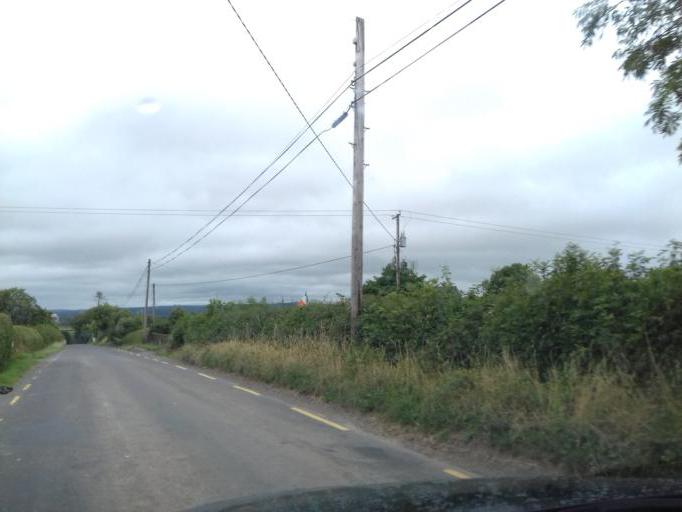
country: IE
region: Leinster
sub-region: County Carlow
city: Bagenalstown
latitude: 52.6209
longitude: -7.0386
